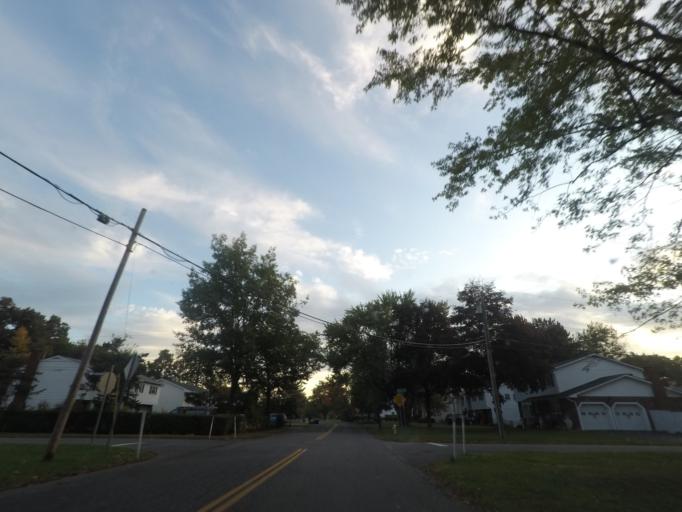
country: US
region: New York
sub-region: Albany County
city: Colonie
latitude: 42.7208
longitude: -73.8268
